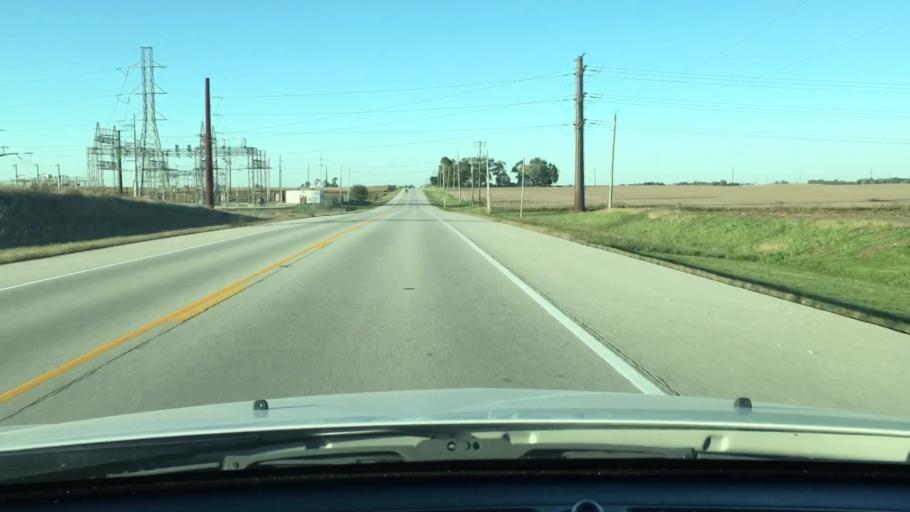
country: US
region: Illinois
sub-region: DeKalb County
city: Waterman
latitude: 41.8257
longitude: -88.7539
